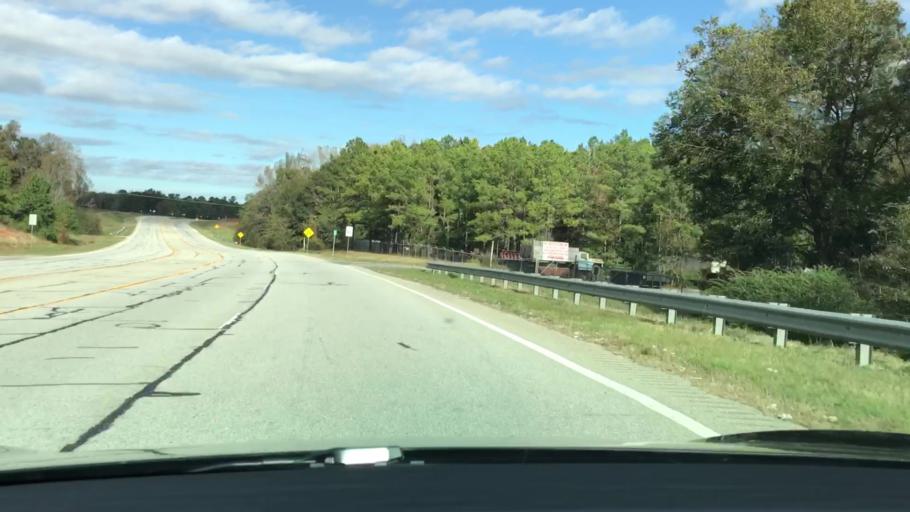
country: US
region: Georgia
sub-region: Jefferson County
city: Wadley
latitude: 32.8859
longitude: -82.3965
